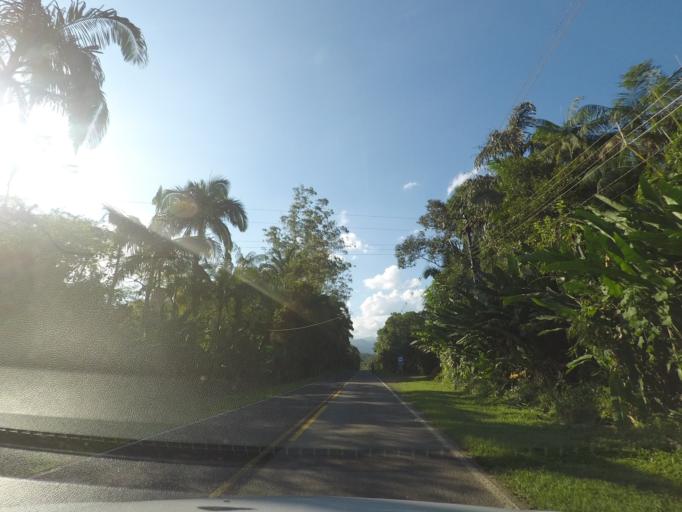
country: BR
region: Parana
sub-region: Antonina
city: Antonina
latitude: -25.4154
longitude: -48.8737
